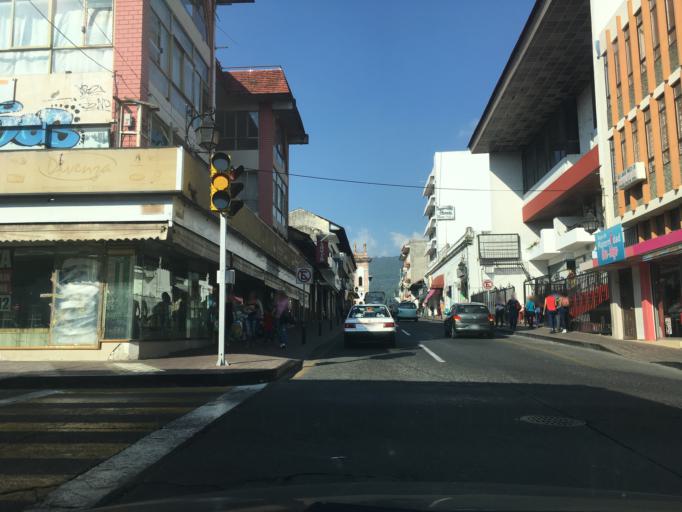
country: MX
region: Michoacan
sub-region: Uruapan
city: Uruapan
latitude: 19.4193
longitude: -102.0621
